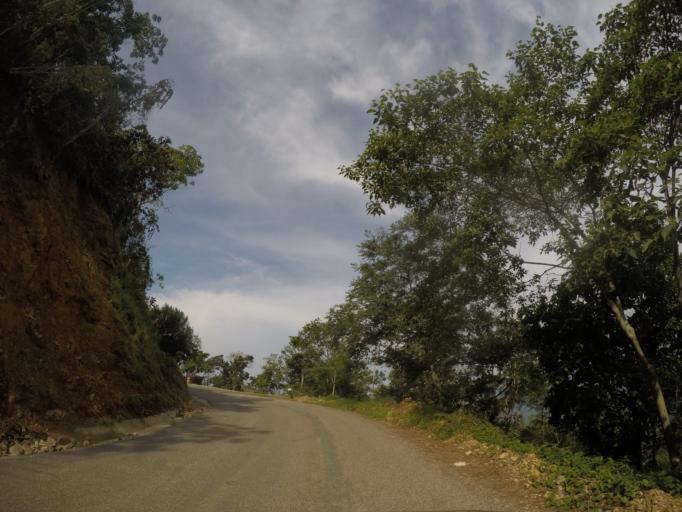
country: MX
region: Oaxaca
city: Pluma Hidalgo
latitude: 15.9426
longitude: -96.4443
